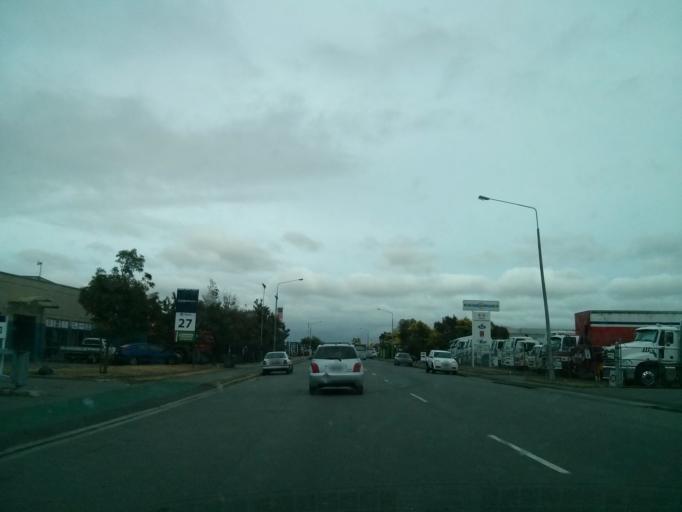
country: NZ
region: Canterbury
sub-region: Selwyn District
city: Prebbleton
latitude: -43.5372
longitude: 172.5443
